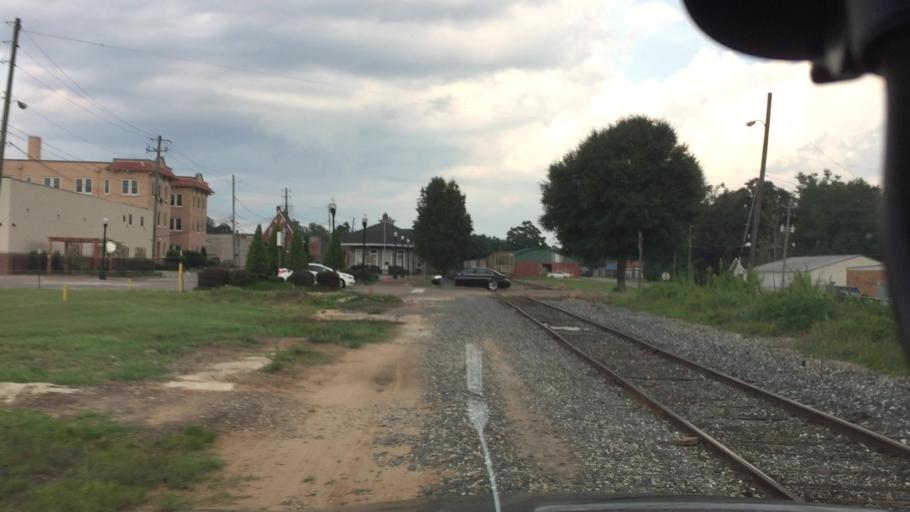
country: US
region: Alabama
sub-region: Coffee County
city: Enterprise
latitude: 31.3144
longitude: -85.8552
